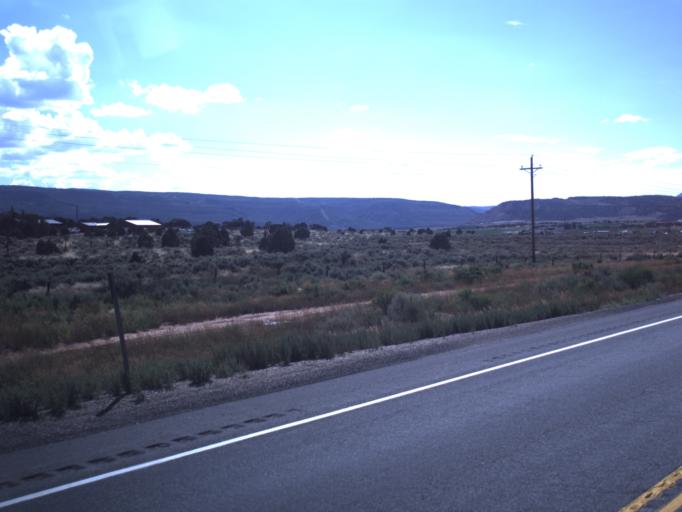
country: US
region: Utah
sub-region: Duchesne County
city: Duchesne
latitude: 40.2093
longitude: -110.8259
